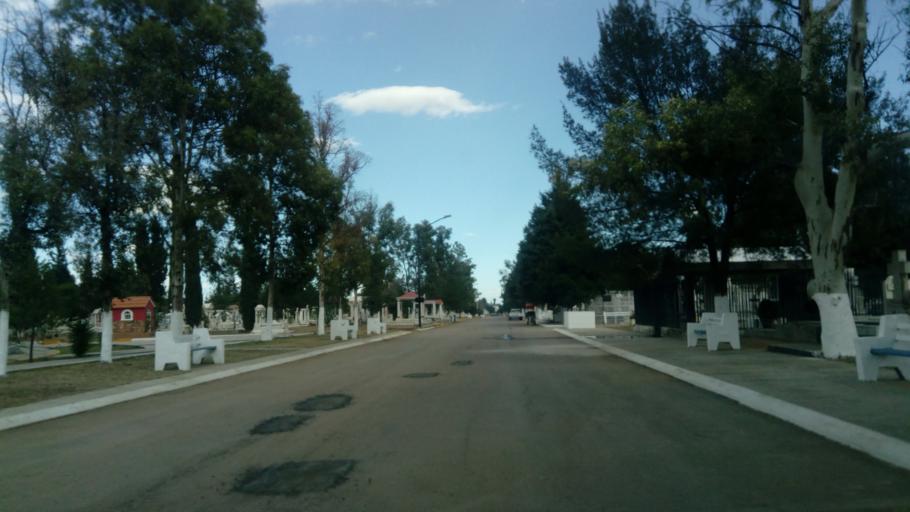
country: MX
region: Durango
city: Victoria de Durango
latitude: 24.0285
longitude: -104.6384
